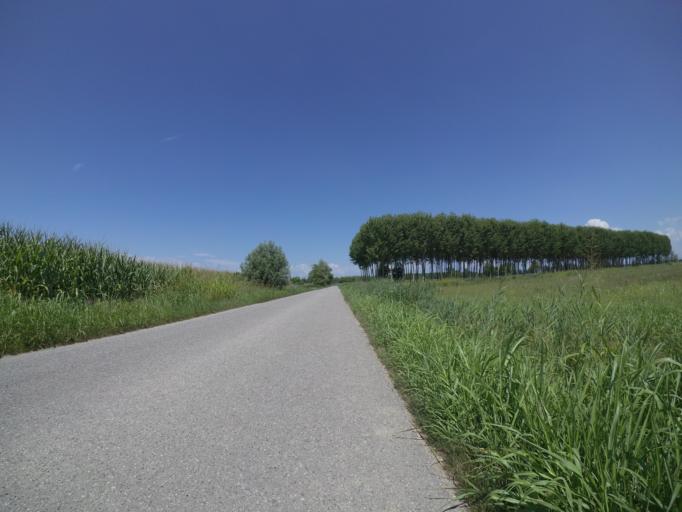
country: IT
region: Friuli Venezia Giulia
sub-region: Provincia di Udine
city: Talmassons
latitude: 45.8996
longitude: 13.1169
